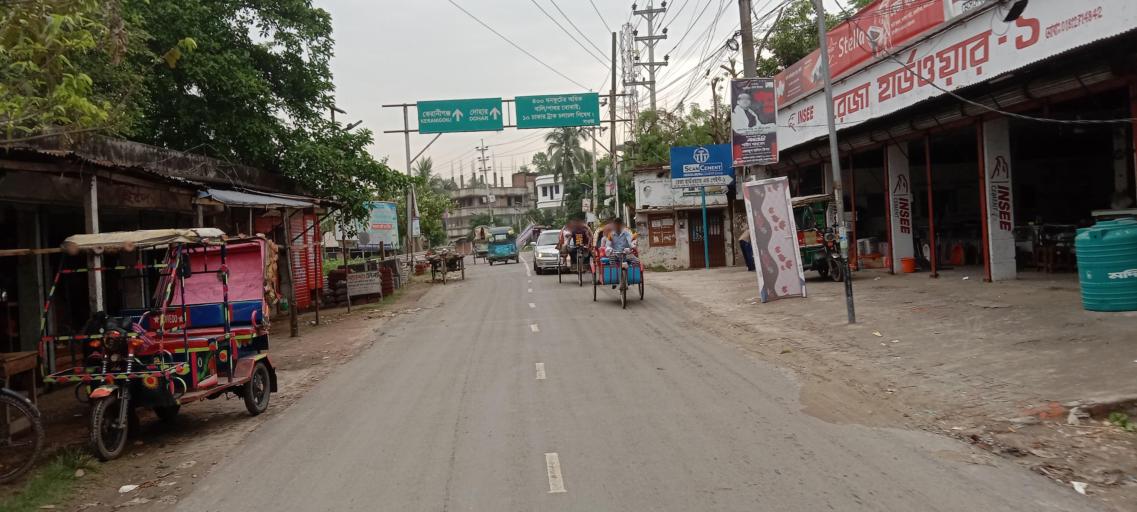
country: BD
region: Dhaka
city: Azimpur
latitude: 23.7318
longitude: 90.3229
